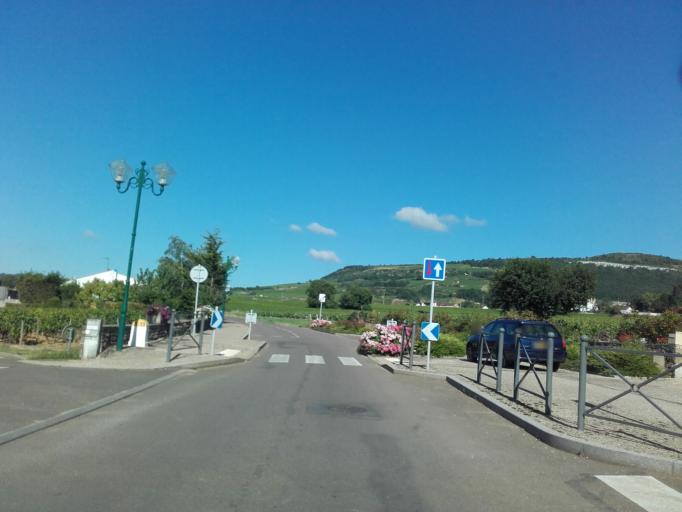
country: FR
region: Bourgogne
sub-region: Departement de Saone-et-Loire
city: Chagny
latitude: 46.9109
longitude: 4.6915
